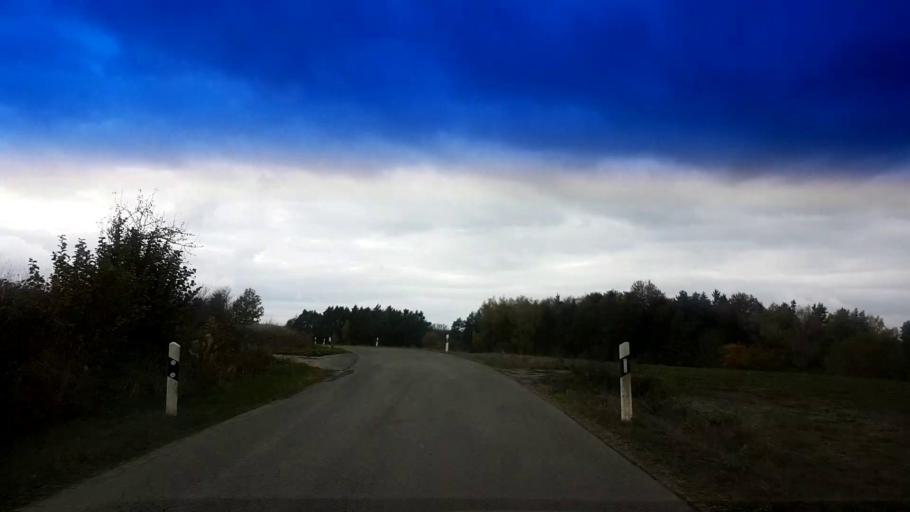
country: DE
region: Bavaria
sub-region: Upper Franconia
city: Wattendorf
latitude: 50.0194
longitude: 11.1160
